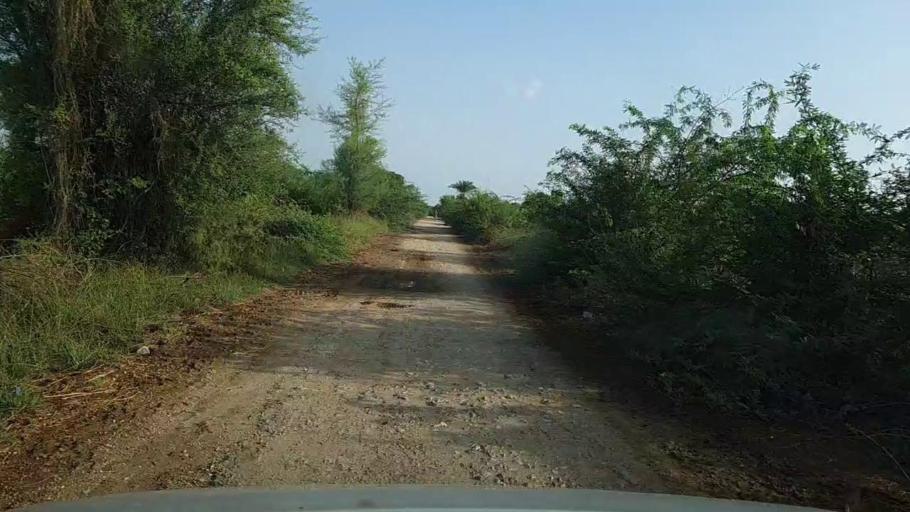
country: PK
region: Sindh
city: Pad Idan
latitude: 26.8103
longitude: 68.2348
